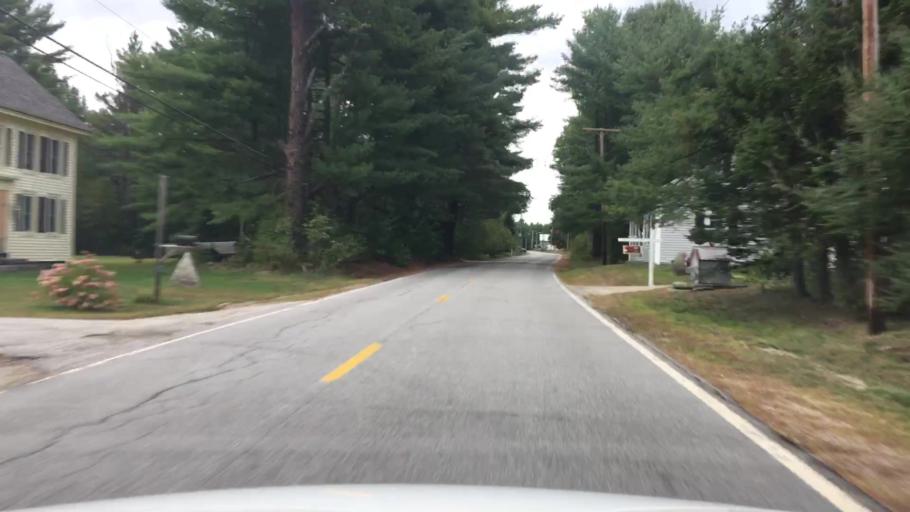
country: US
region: New Hampshire
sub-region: Carroll County
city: Effingham
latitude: 43.7076
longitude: -70.9820
